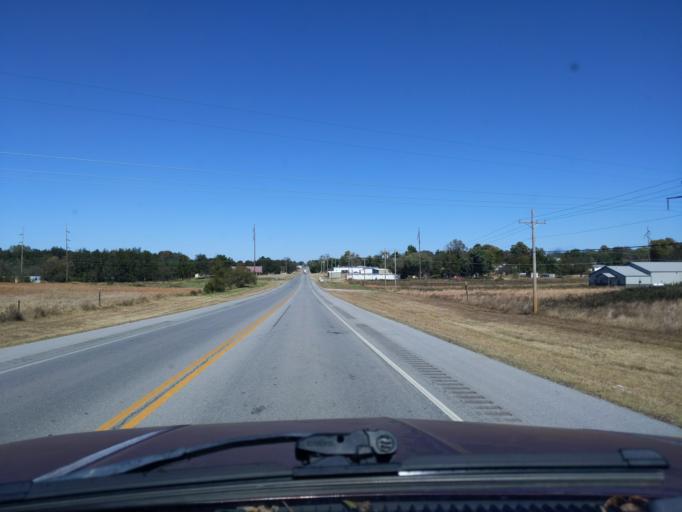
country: US
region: Oklahoma
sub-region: Creek County
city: Bristow
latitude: 35.8114
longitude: -96.3872
